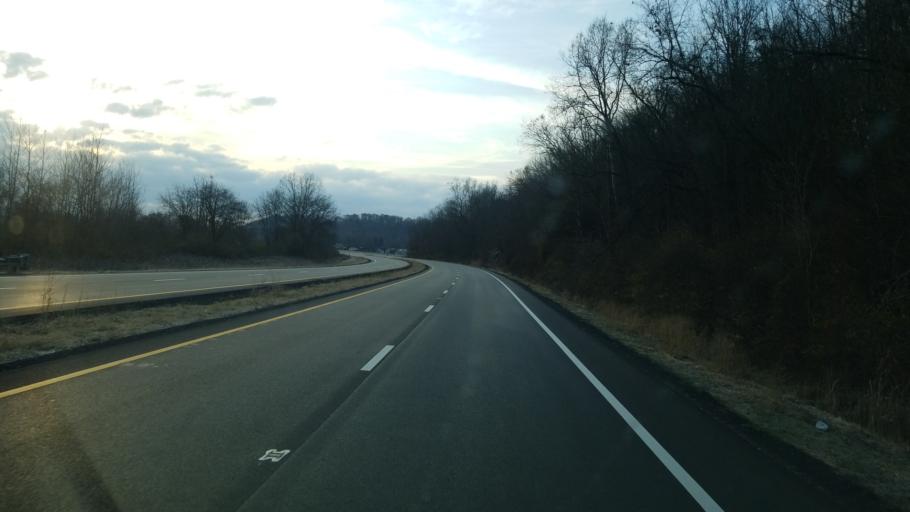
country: US
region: Ohio
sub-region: Ross County
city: Chillicothe
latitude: 39.3030
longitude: -82.9581
